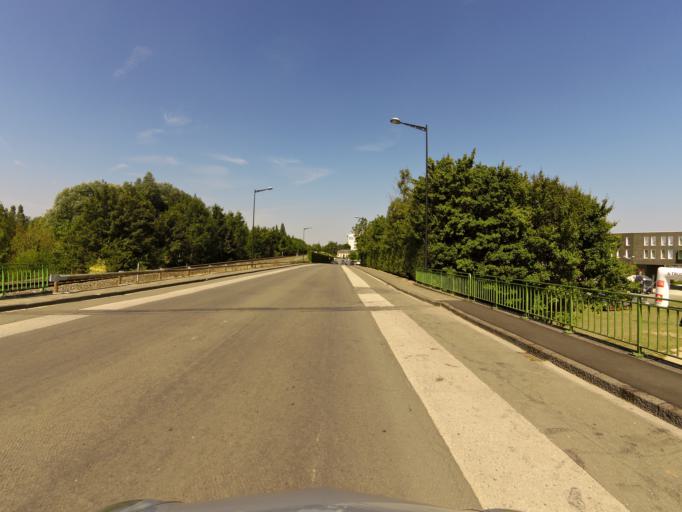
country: BE
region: Flanders
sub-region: Provincie Oost-Vlaanderen
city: Oudenaarde
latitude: 50.8395
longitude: 3.6033
